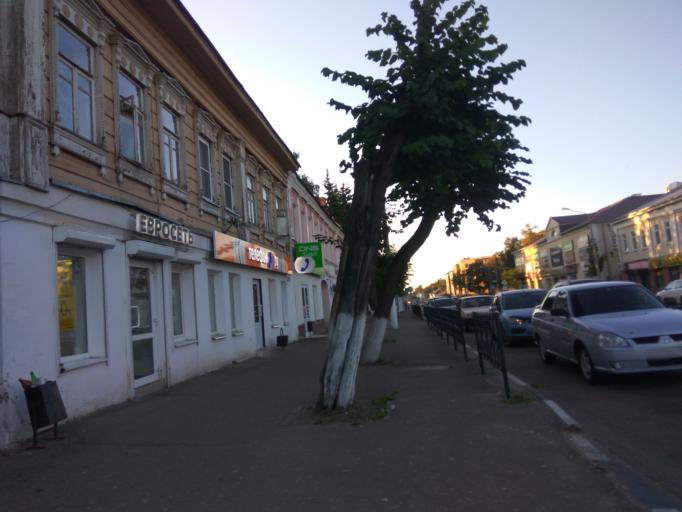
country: RU
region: Moskovskaya
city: Yegor'yevsk
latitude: 55.3802
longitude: 39.0401
